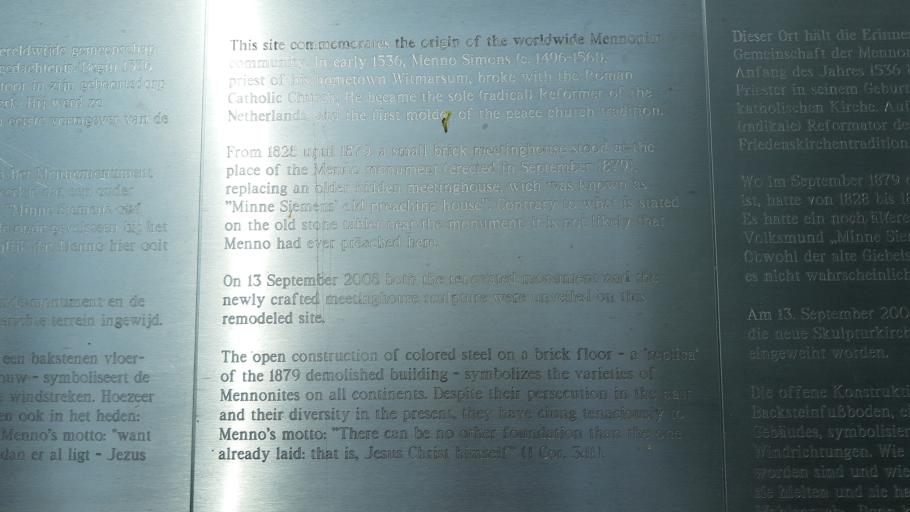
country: NL
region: Friesland
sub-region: Sudwest Fryslan
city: Bolsward
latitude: 53.0994
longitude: 5.4822
